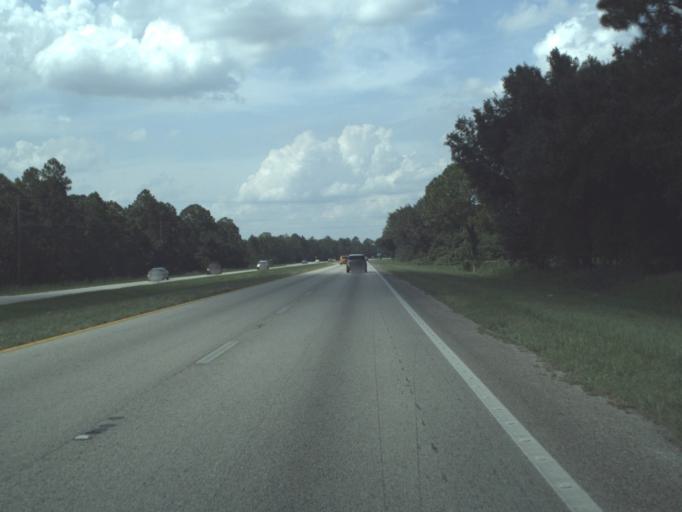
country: US
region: Florida
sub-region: Polk County
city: Frostproof
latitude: 27.7615
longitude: -81.5920
